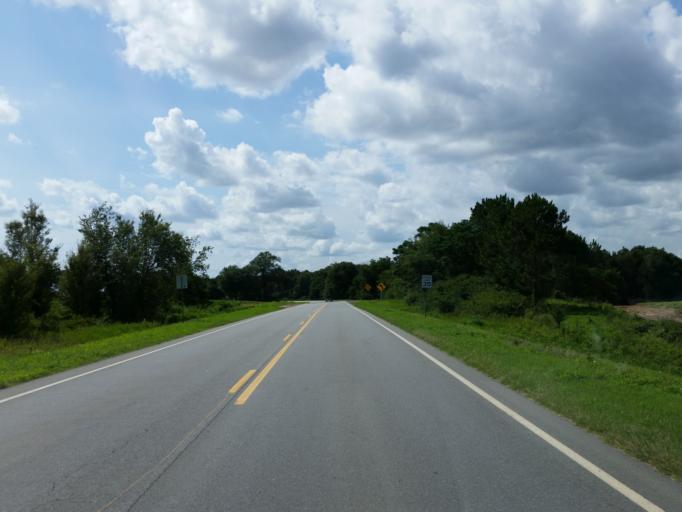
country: US
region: Georgia
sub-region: Turner County
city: Ashburn
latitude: 31.6626
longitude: -83.6015
